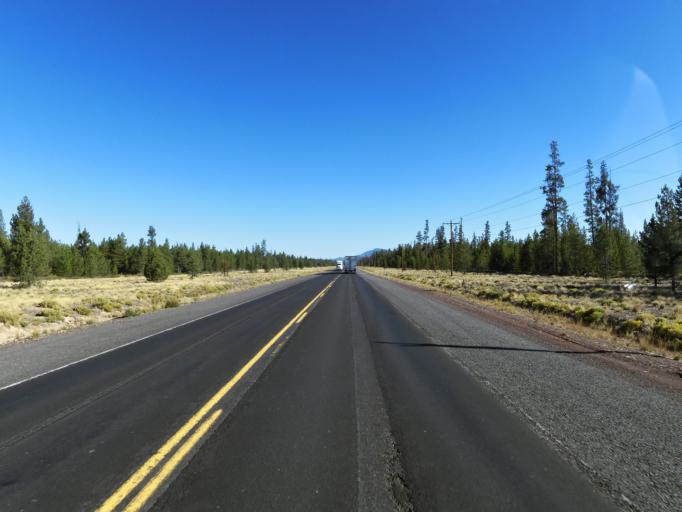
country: US
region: Oregon
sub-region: Deschutes County
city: La Pine
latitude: 43.1472
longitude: -121.7976
